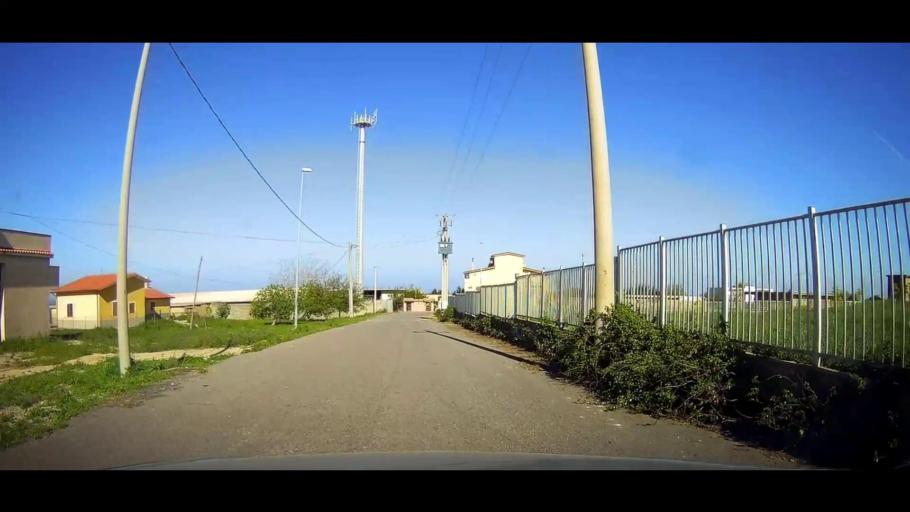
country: IT
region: Calabria
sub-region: Provincia di Crotone
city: Crotone
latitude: 39.0321
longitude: 17.1608
